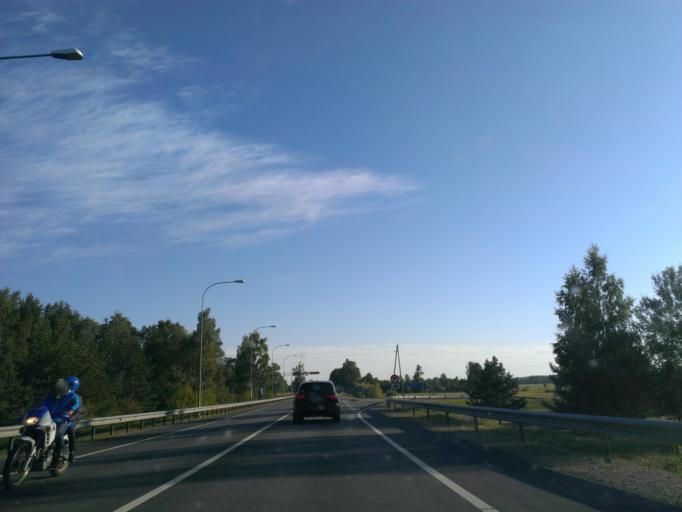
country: LV
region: Adazi
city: Adazi
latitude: 57.1186
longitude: 24.3246
